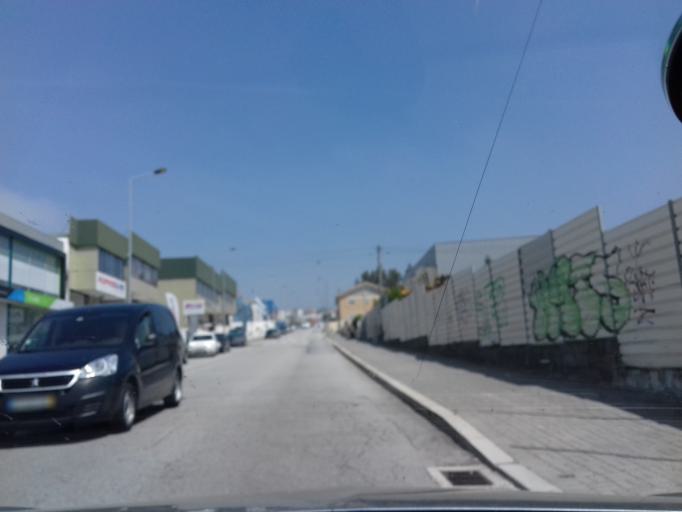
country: PT
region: Porto
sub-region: Vila Nova de Gaia
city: Canelas
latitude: 41.0907
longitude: -8.6037
